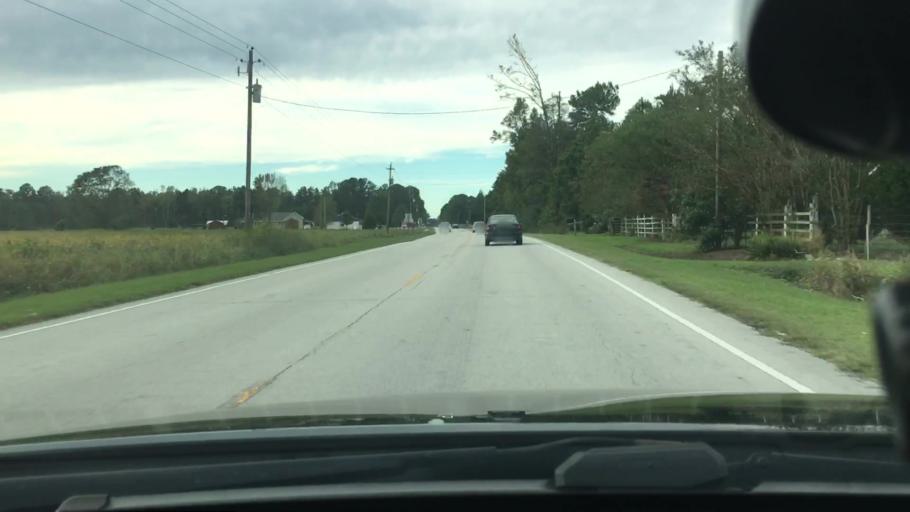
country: US
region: North Carolina
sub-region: Craven County
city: Vanceboro
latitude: 35.3394
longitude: -77.1764
